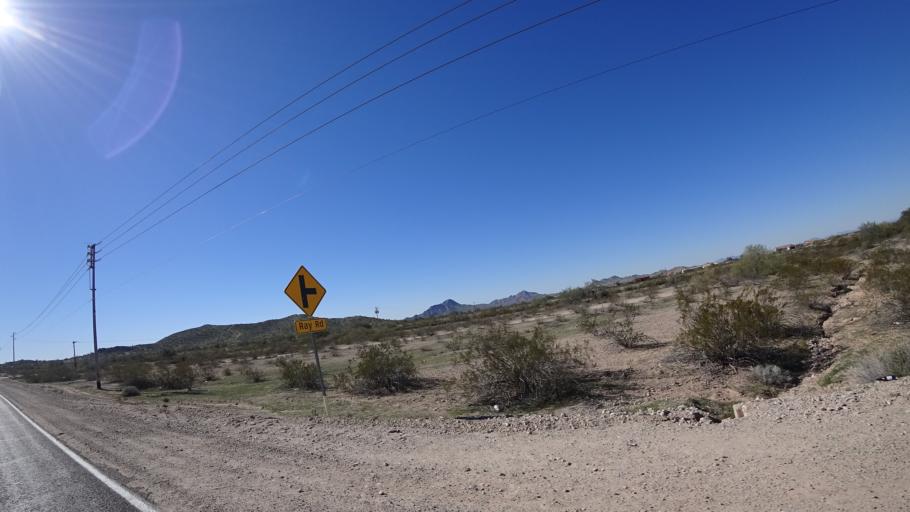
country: US
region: Arizona
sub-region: Maricopa County
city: Buckeye
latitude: 33.3211
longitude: -112.4699
